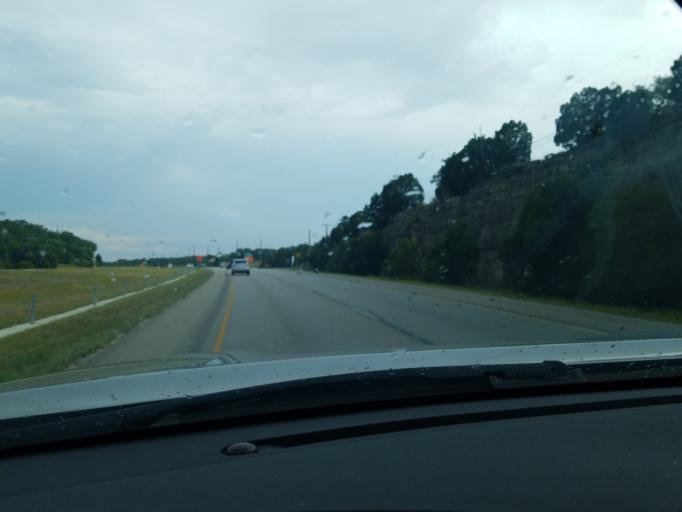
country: US
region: Texas
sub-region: Comal County
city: Bulverde
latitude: 29.7774
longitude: -98.4262
